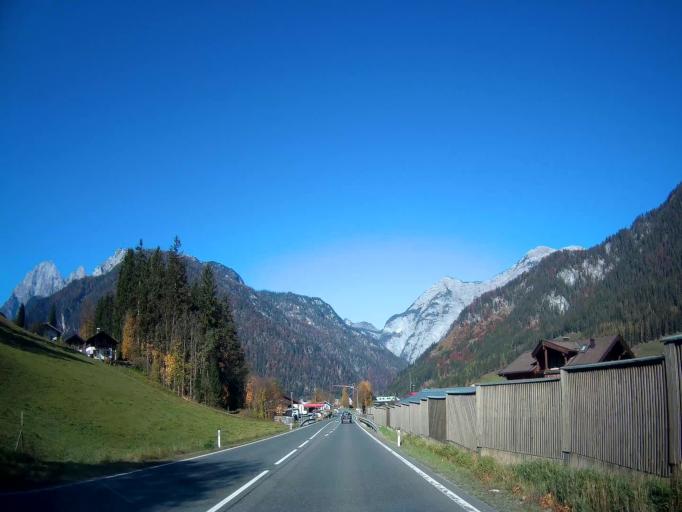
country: AT
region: Salzburg
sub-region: Politischer Bezirk Zell am See
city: Saalfelden am Steinernen Meer
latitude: 47.4500
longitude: 12.8345
